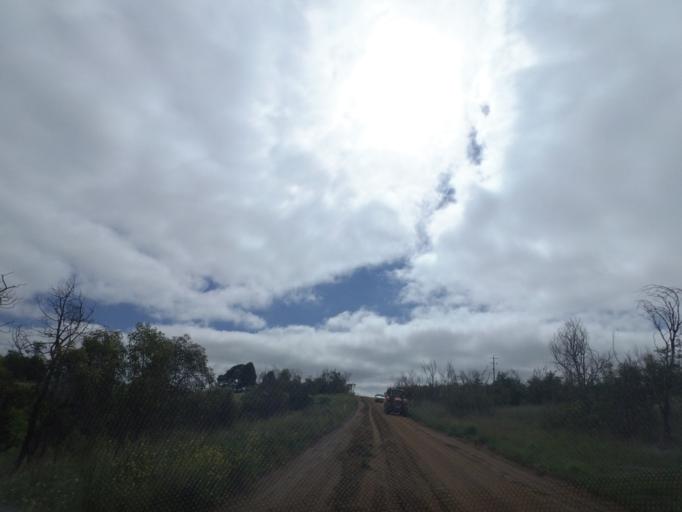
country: AU
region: Victoria
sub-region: Hume
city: Craigieburn
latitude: -37.5036
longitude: 144.8986
